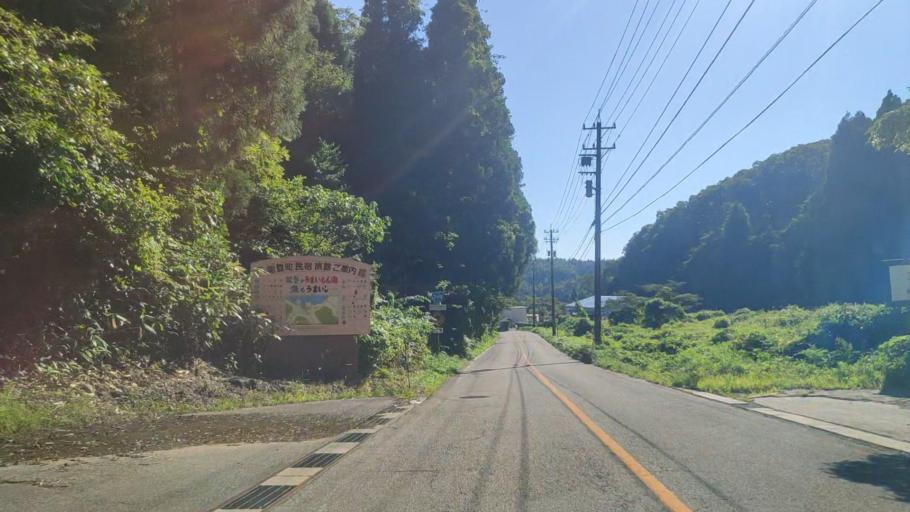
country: JP
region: Ishikawa
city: Nanao
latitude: 37.3195
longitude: 137.1657
